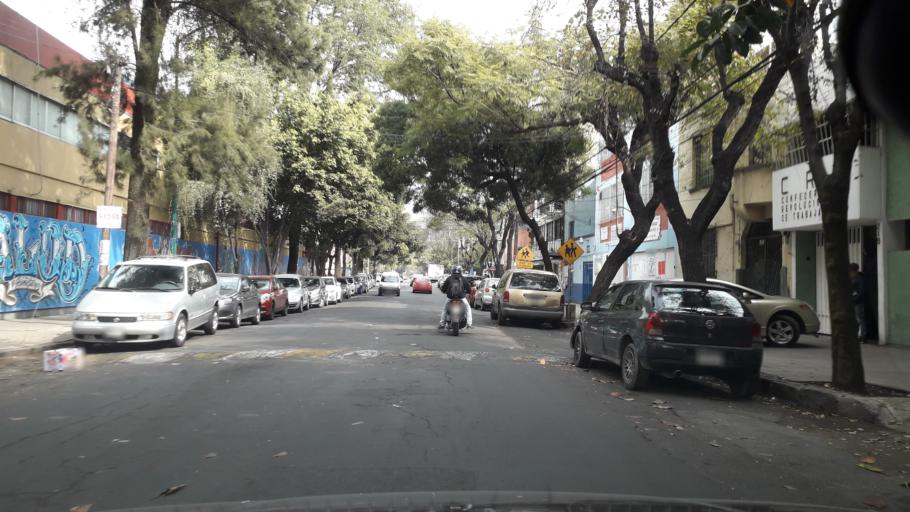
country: MX
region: Mexico City
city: Benito Juarez
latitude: 19.4137
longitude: -99.1502
